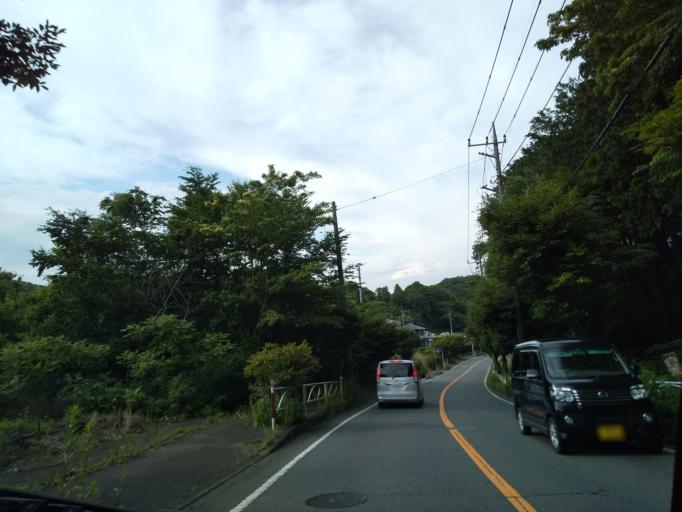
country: JP
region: Kanagawa
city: Atsugi
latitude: 35.4809
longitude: 139.3183
